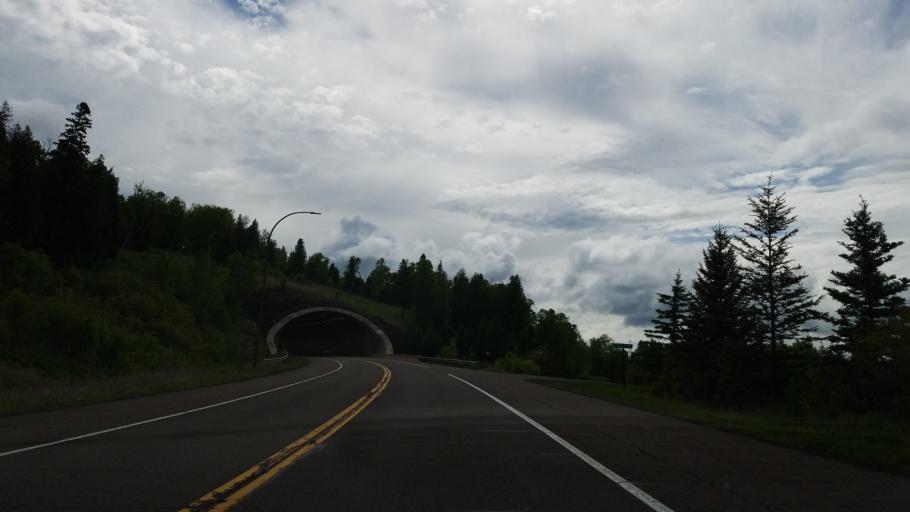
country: US
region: Minnesota
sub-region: Lake County
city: Two Harbors
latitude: 47.0953
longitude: -91.5562
